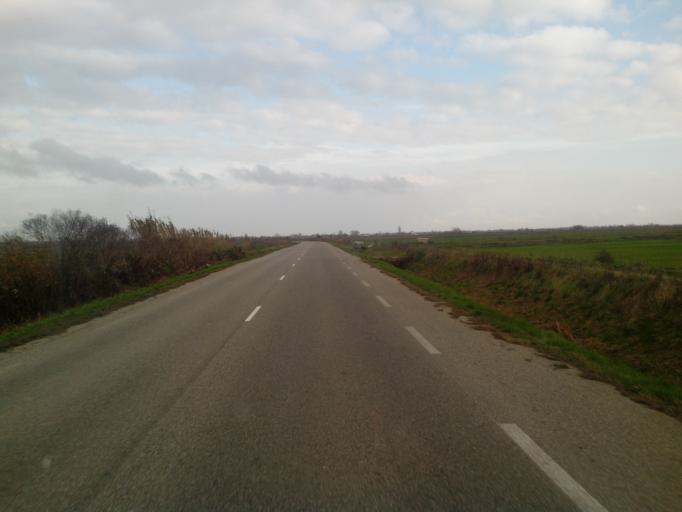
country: FR
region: Provence-Alpes-Cote d'Azur
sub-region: Departement des Bouches-du-Rhone
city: Saintes-Maries-de-la-Mer
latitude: 43.5462
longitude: 4.3695
